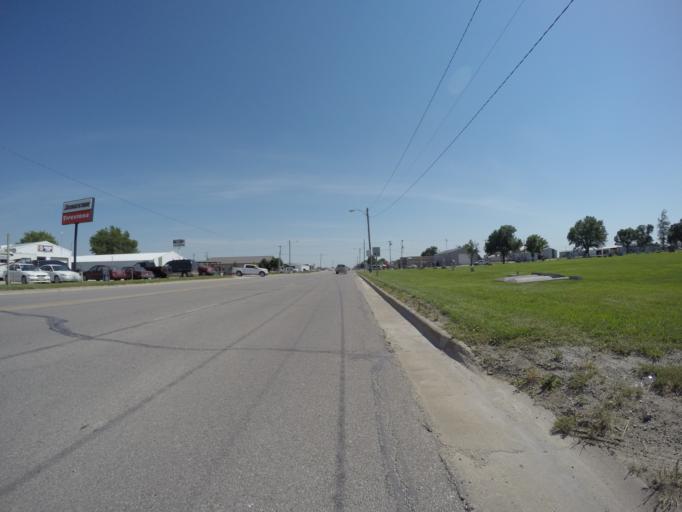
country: US
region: Kansas
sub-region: Nemaha County
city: Sabetha
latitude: 39.9006
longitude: -95.7883
